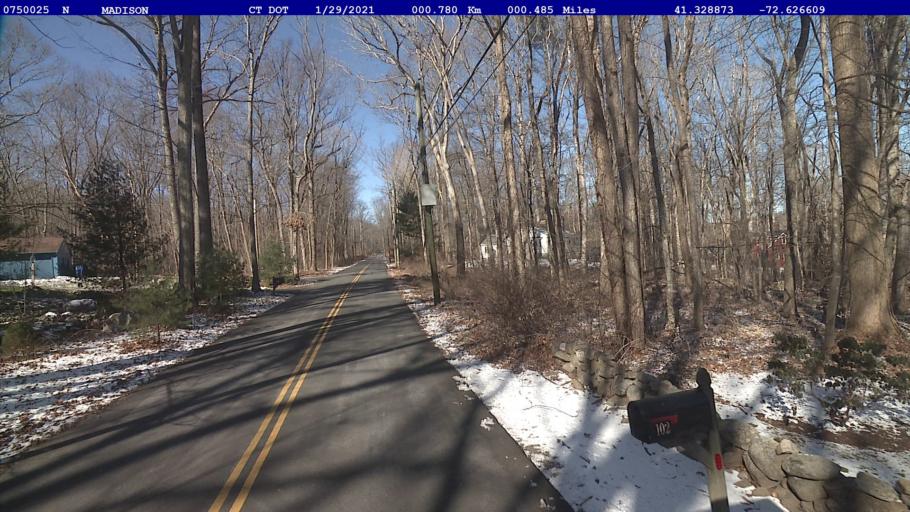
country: US
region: Connecticut
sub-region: New Haven County
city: Madison Center
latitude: 41.3289
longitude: -72.6266
